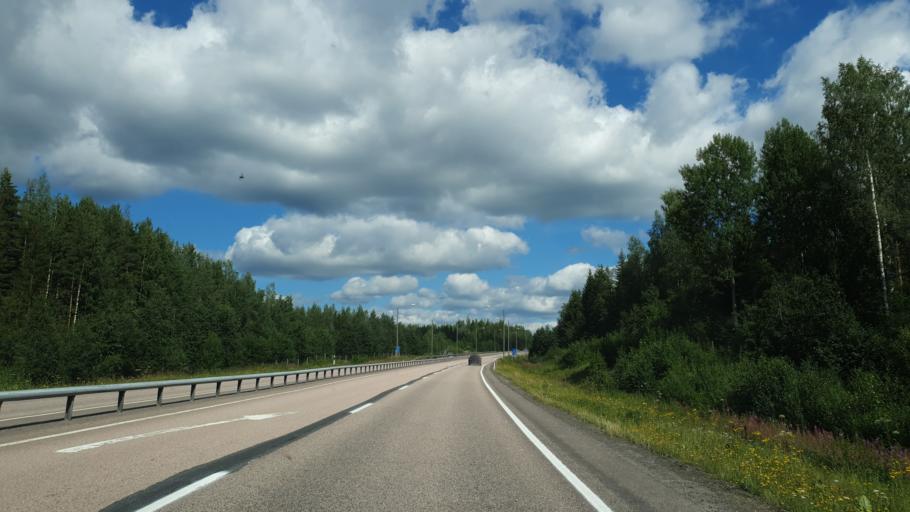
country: FI
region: Central Finland
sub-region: Jaemsae
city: Jaemsae
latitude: 61.8166
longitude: 25.0130
